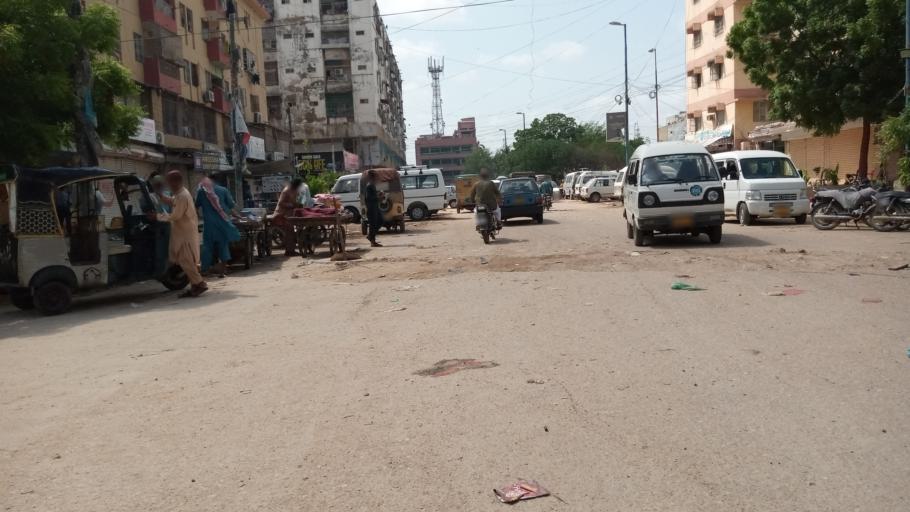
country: PK
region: Sindh
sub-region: Karachi District
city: Karachi
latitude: 24.9280
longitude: 67.0672
